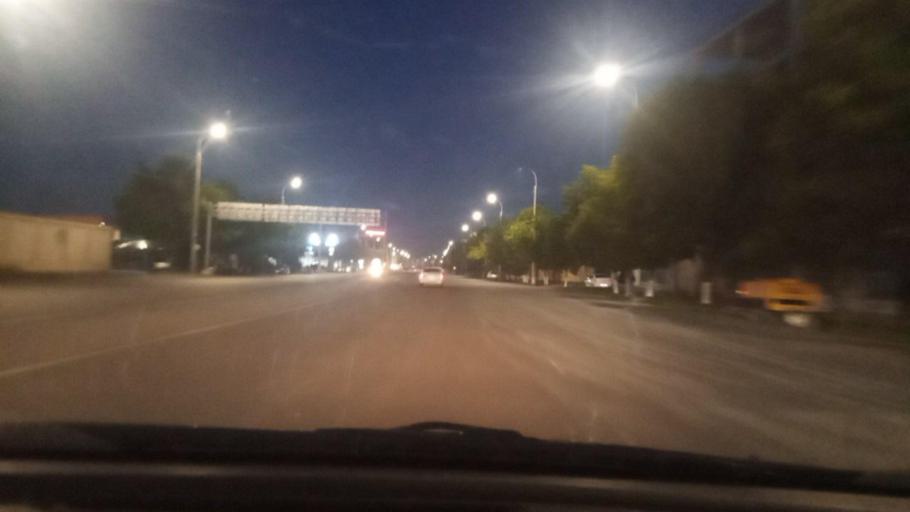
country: UZ
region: Toshkent Shahri
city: Tashkent
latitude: 41.2648
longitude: 69.2368
